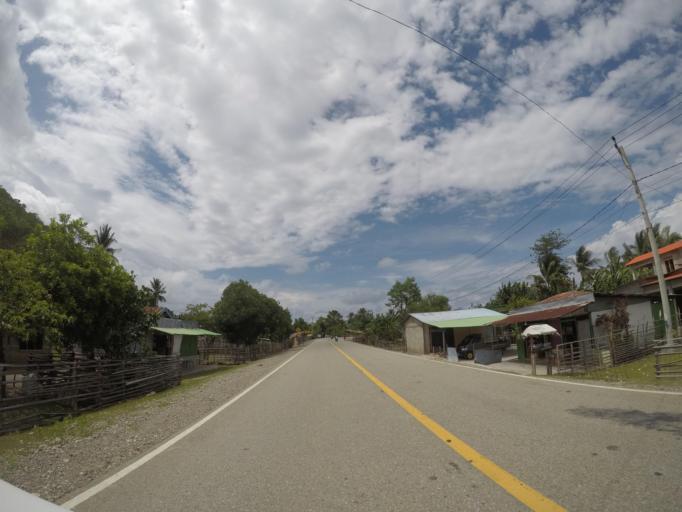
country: TL
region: Bobonaro
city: Maliana
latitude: -8.8321
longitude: 125.0565
